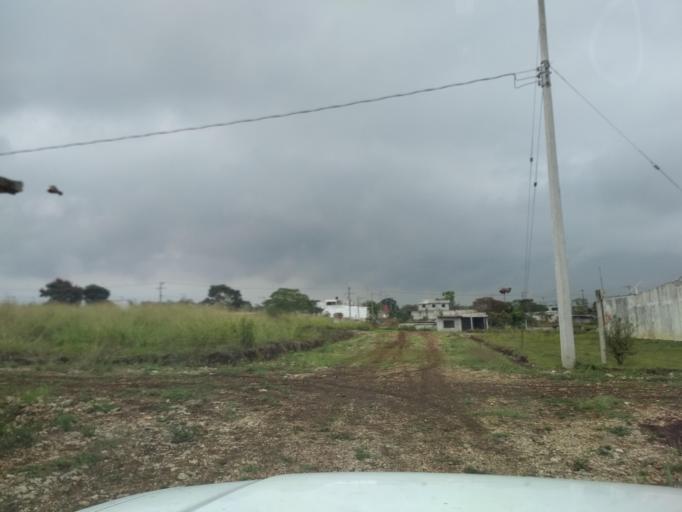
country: MX
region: Veracruz
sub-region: Cordoba
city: San Jose de Tapia
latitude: 18.8433
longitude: -96.9680
